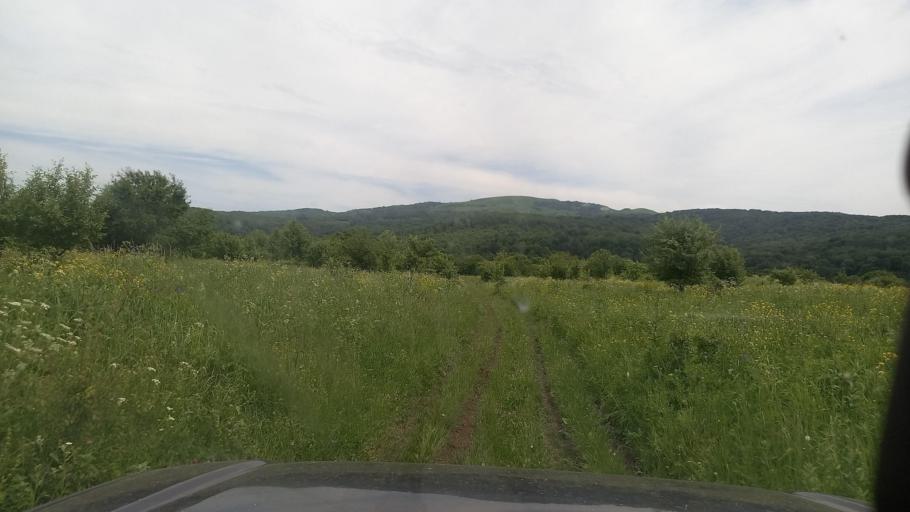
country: RU
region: Karachayevo-Cherkesiya
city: Pregradnaya
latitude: 44.1015
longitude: 41.1938
